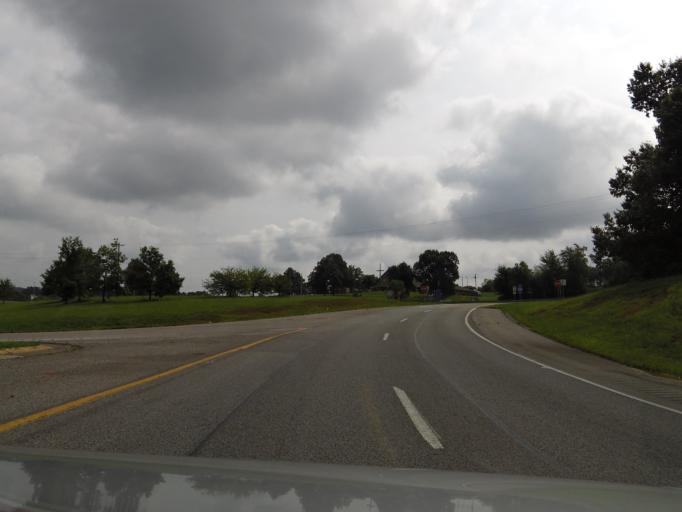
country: US
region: Kentucky
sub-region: Hopkins County
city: Madisonville
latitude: 37.3674
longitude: -87.4933
